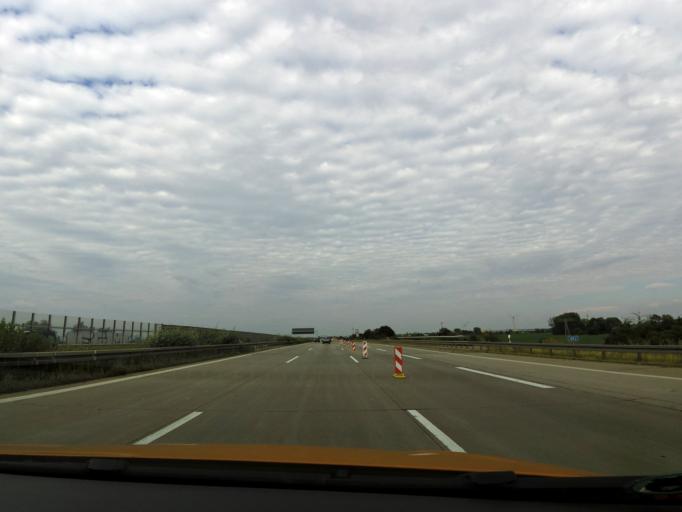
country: DE
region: Saxony-Anhalt
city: Barleben
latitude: 52.1919
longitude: 11.6315
